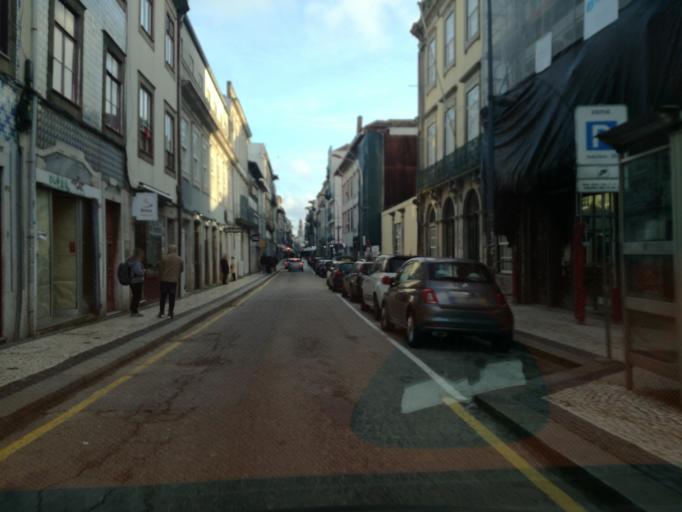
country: PT
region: Porto
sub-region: Porto
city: Porto
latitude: 41.1522
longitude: -8.6179
